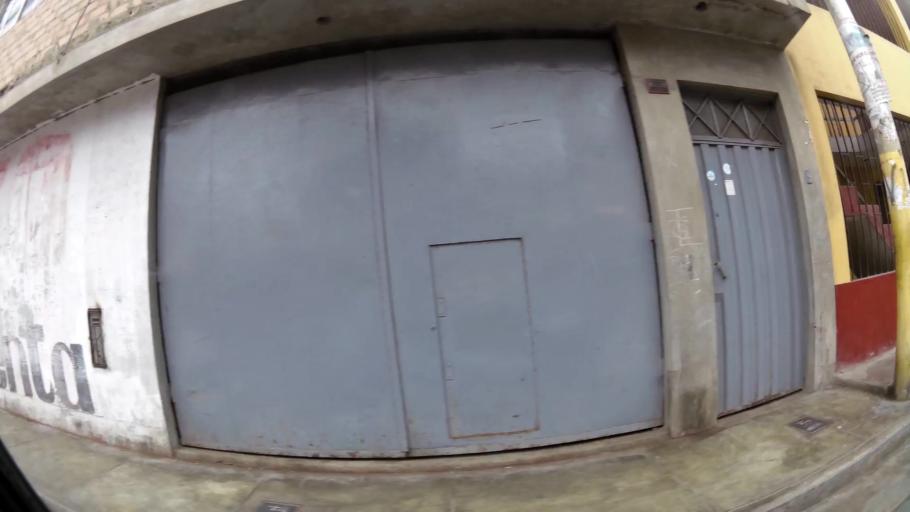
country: PE
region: Lima
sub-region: Barranca
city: Barranca
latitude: -10.7485
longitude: -77.7553
